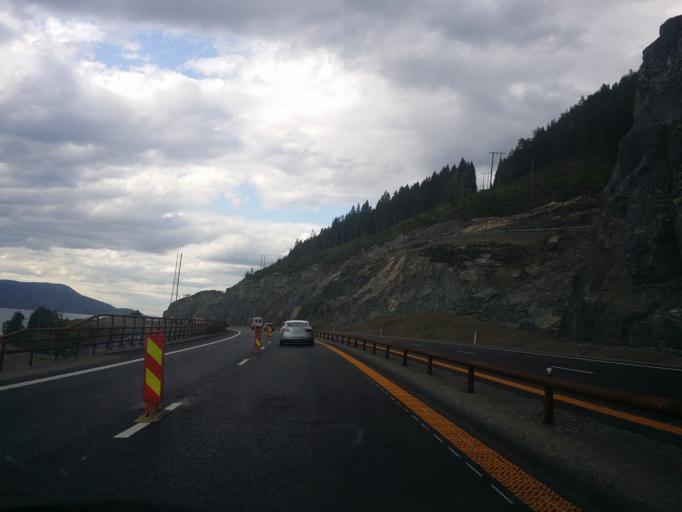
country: NO
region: Akershus
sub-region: Eidsvoll
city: Eidsvoll
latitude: 60.4483
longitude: 11.2425
